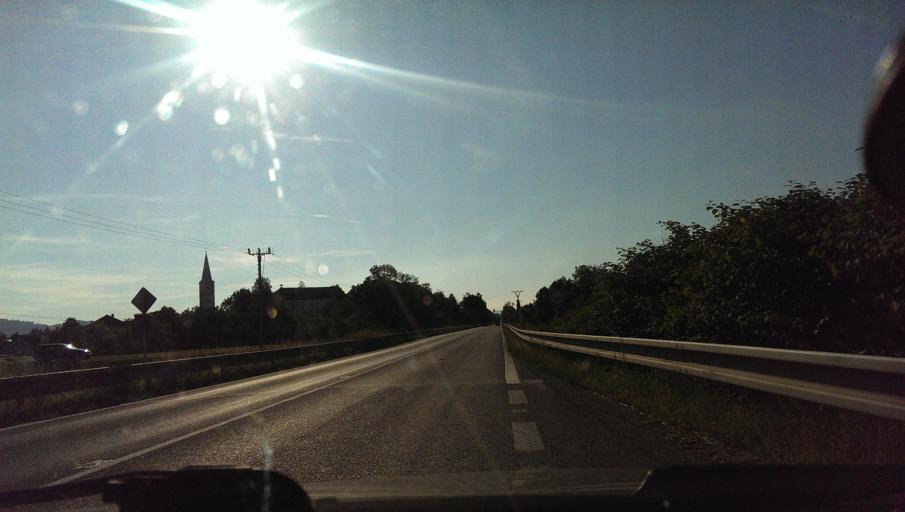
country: CZ
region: Olomoucky
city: Hustopece Nad Becvou
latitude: 49.5307
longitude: 17.8645
